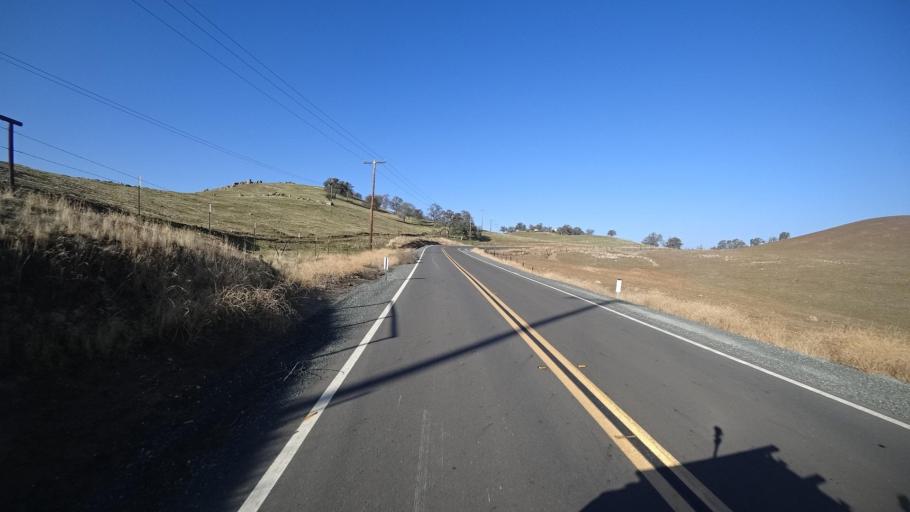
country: US
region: California
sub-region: Tulare County
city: Richgrove
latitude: 35.7116
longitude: -118.8432
